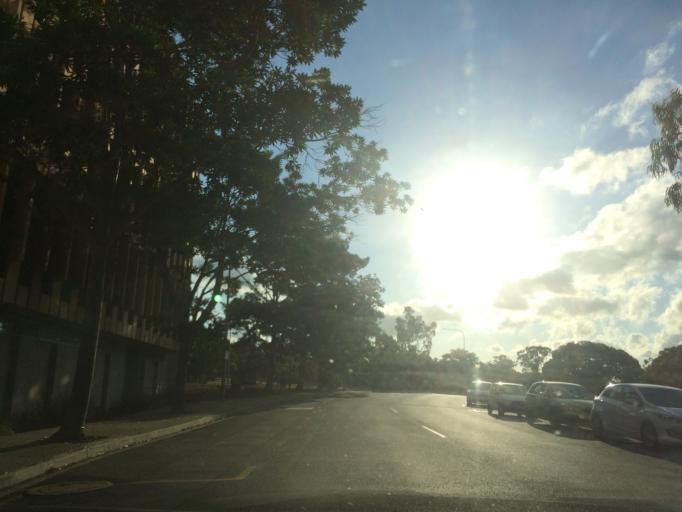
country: AU
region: Queensland
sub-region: Brisbane
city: South Brisbane
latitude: -27.4945
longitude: 153.0139
